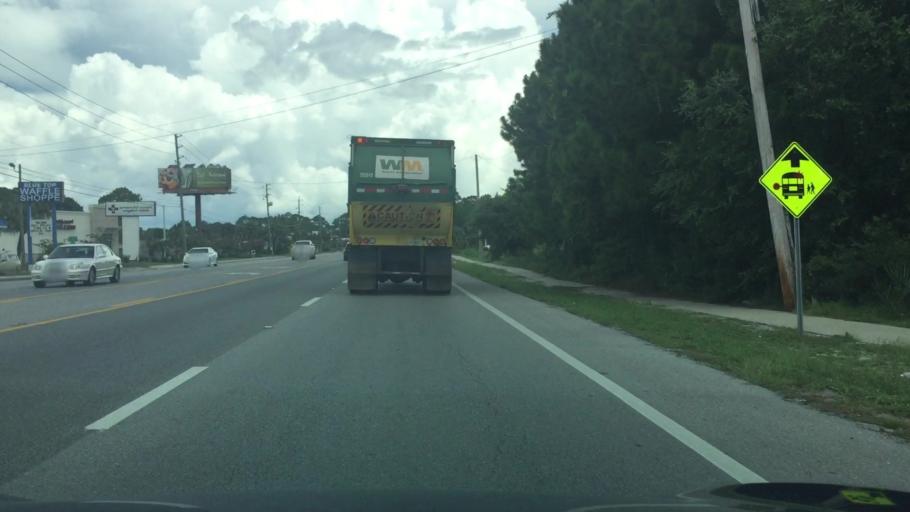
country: US
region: Florida
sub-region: Bay County
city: Lower Grand Lagoon
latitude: 30.1546
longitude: -85.7511
